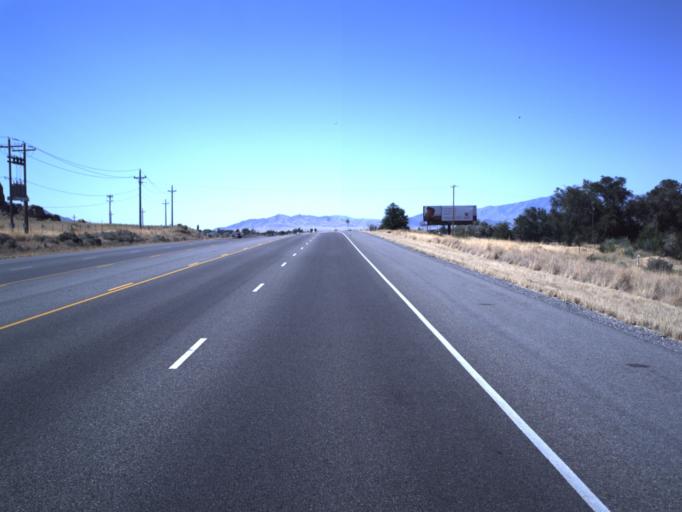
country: US
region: Utah
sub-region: Tooele County
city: Stansbury park
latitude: 40.6628
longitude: -112.2880
